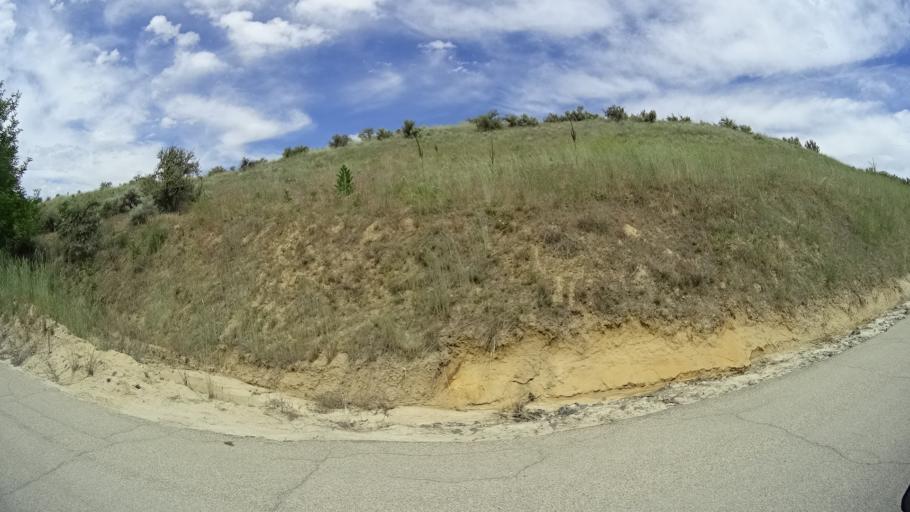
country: US
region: Idaho
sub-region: Ada County
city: Boise
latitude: 43.6404
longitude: -116.1935
